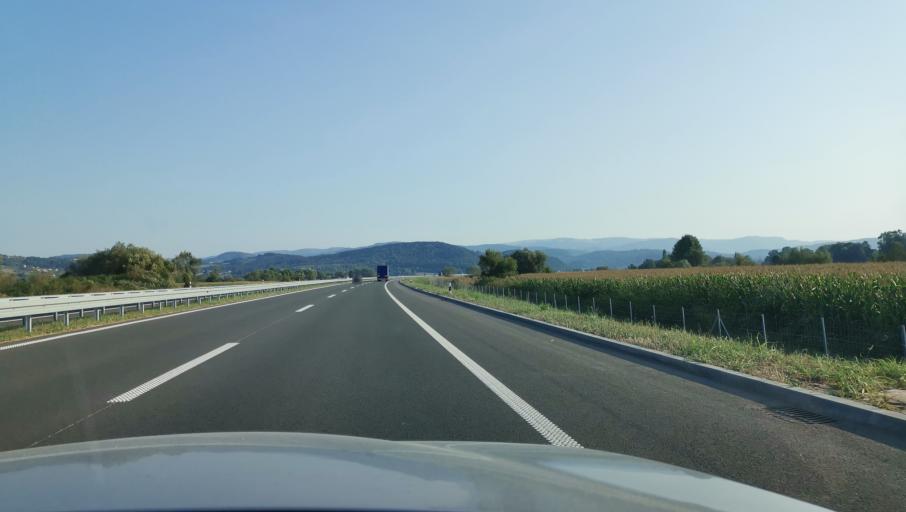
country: RS
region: Central Serbia
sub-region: Kolubarski Okrug
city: Ljig
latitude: 44.2593
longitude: 20.2709
